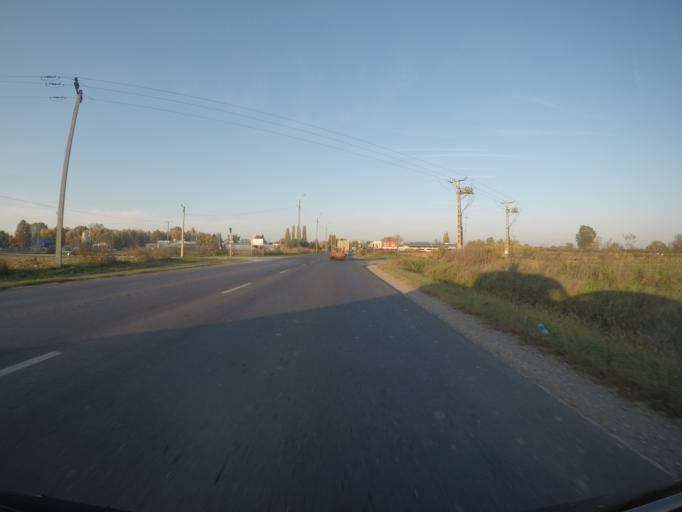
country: HU
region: Baranya
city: Szigetvar
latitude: 46.0458
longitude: 17.8180
